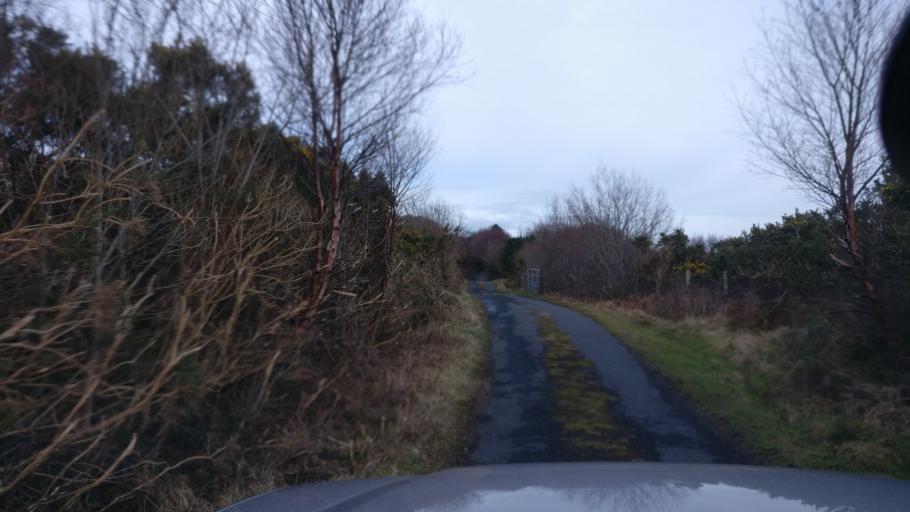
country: IE
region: Connaught
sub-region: County Galway
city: Oughterard
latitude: 53.5202
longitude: -9.4291
